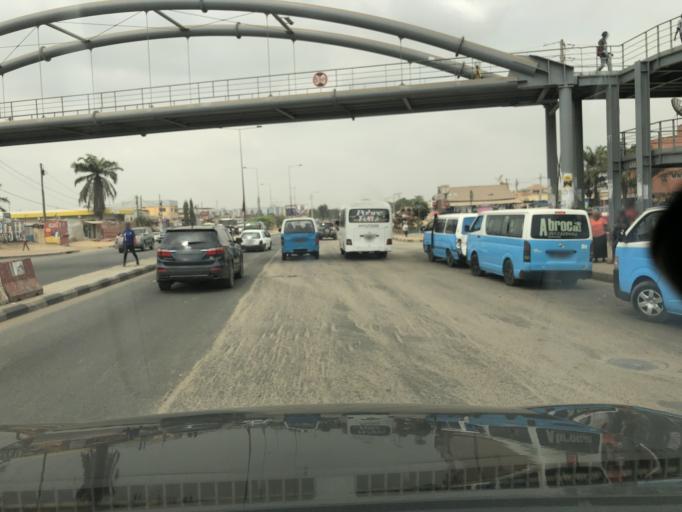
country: AO
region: Luanda
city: Luanda
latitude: -8.8388
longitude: 13.2838
